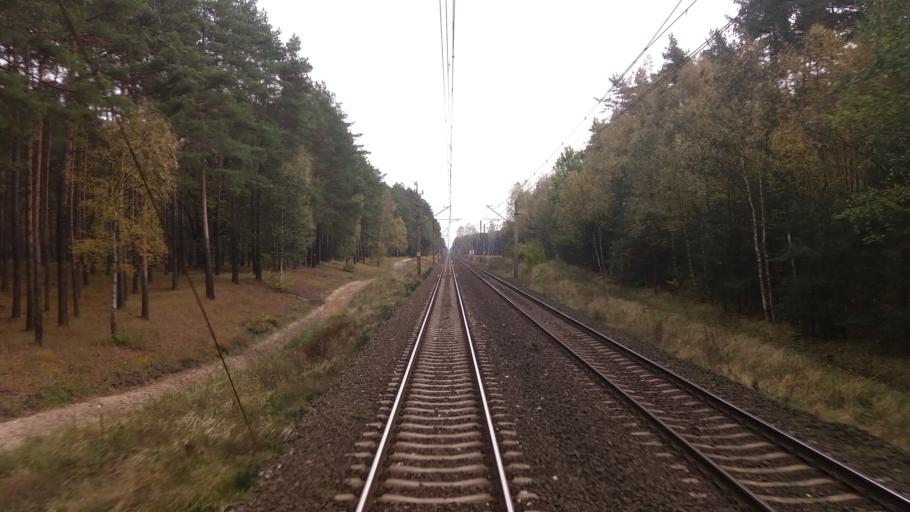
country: PL
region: West Pomeranian Voivodeship
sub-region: Powiat stargardzki
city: Kobylanka
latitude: 53.3799
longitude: 14.7968
